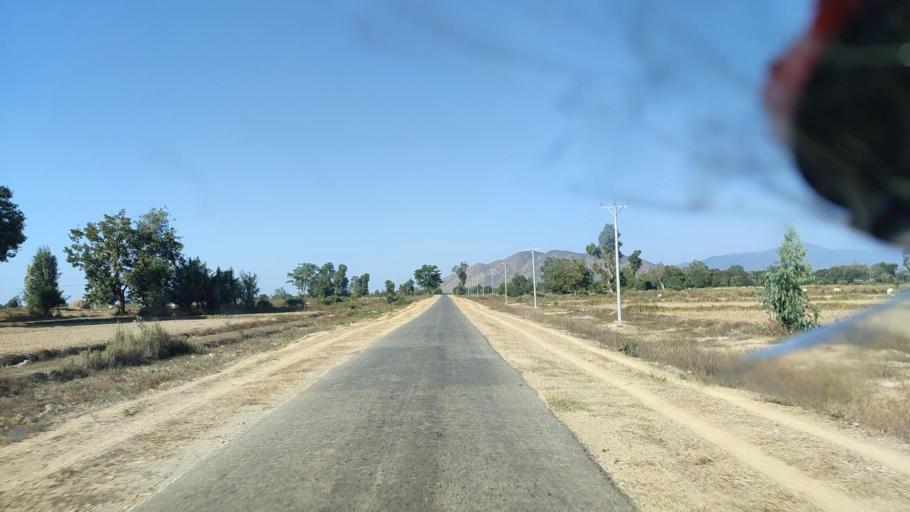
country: MM
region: Mandalay
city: Yamethin
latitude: 20.2263
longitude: 96.2622
